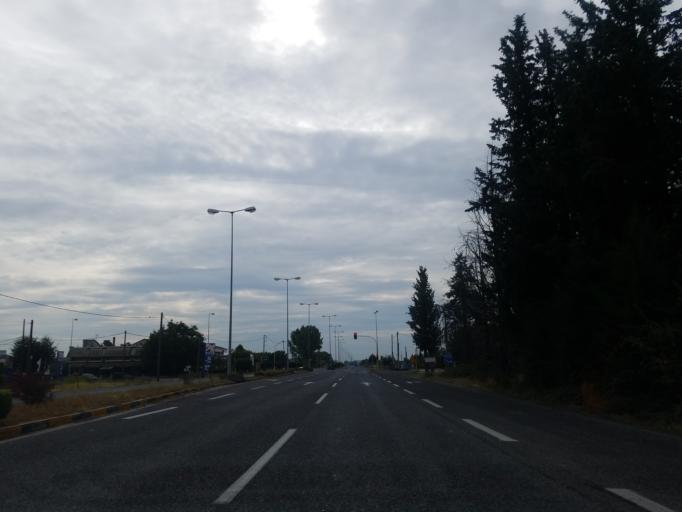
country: GR
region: Thessaly
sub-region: Trikala
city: Vasiliki
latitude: 39.6354
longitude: 21.6986
